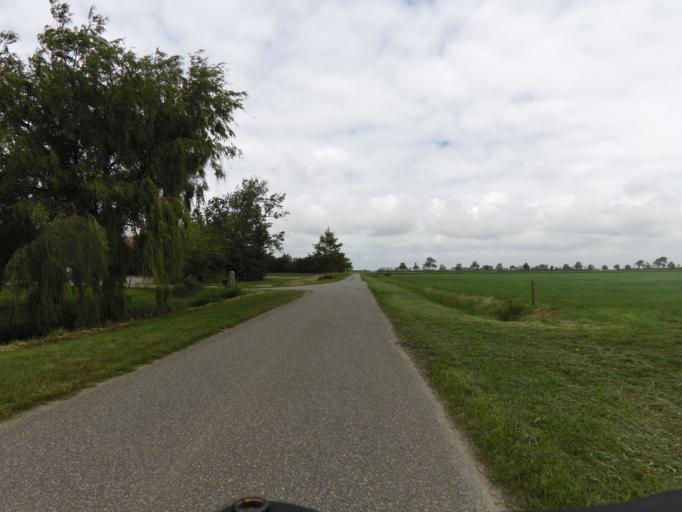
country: NL
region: Zeeland
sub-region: Schouwen-Duiveland
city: Bruinisse
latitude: 51.6304
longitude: 3.9605
